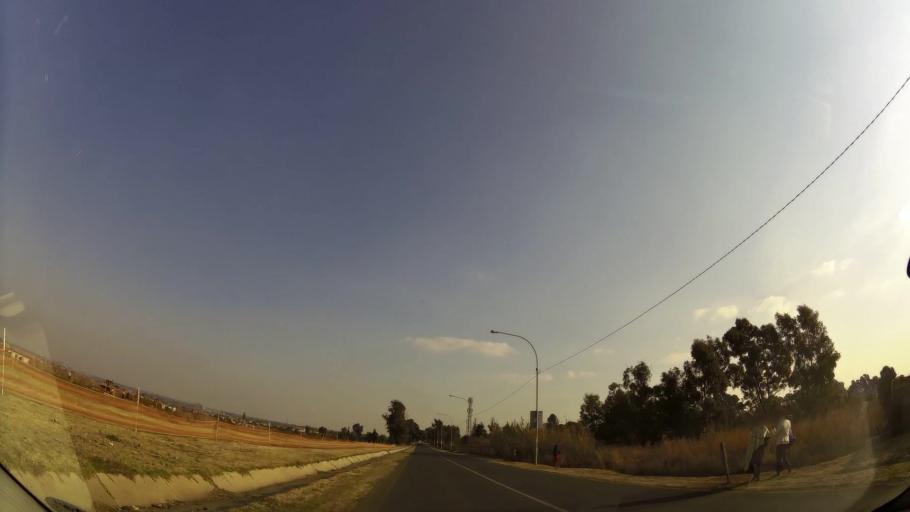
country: ZA
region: Gauteng
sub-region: Ekurhuleni Metropolitan Municipality
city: Benoni
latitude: -26.1468
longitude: 28.3849
